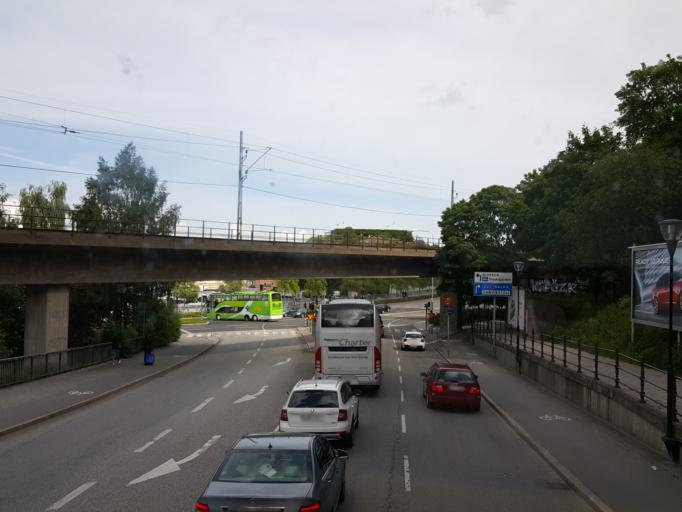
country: SE
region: Stockholm
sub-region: Stockholms Kommun
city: OEstermalm
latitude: 59.3154
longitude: 18.0936
